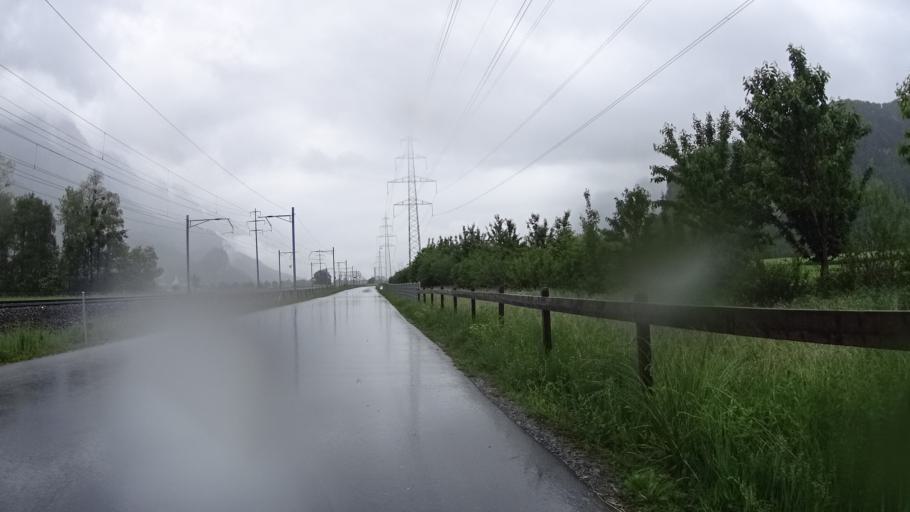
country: CH
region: Saint Gallen
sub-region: Wahlkreis Sarganserland
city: Walenstadt
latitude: 47.1121
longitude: 9.3280
